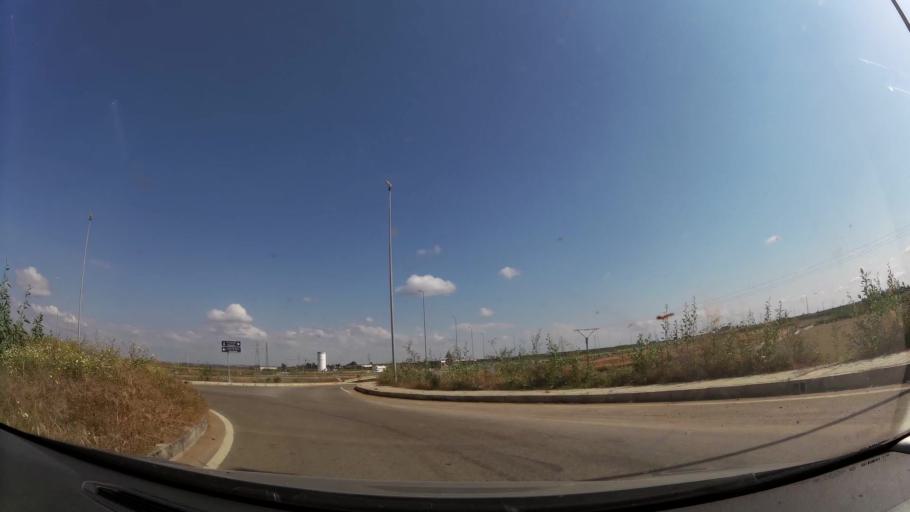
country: MA
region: Rabat-Sale-Zemmour-Zaer
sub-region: Rabat
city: Rabat
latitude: 33.9094
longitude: -6.7787
